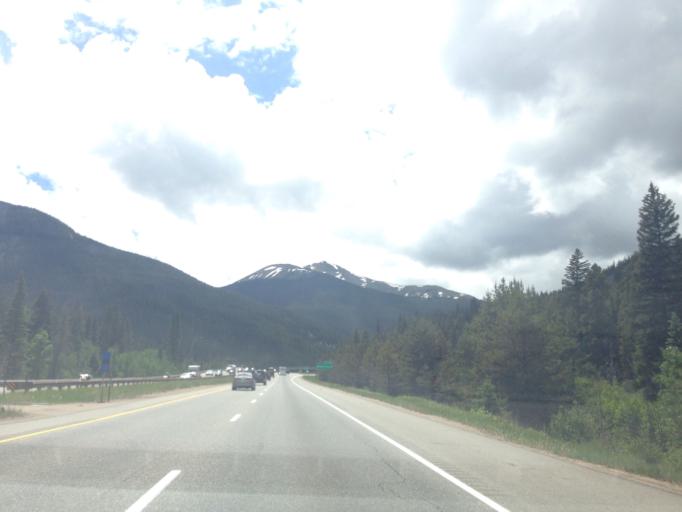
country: US
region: Colorado
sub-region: Clear Creek County
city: Georgetown
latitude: 39.6945
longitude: -105.7988
